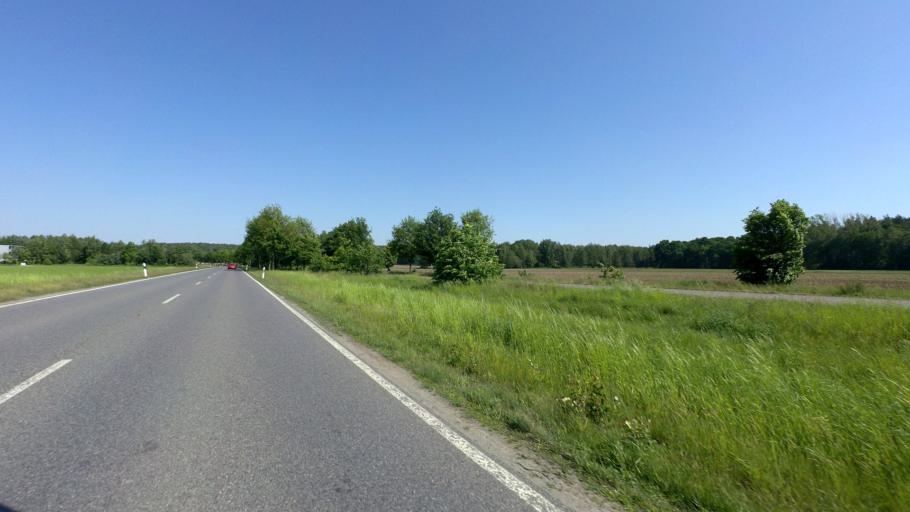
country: DE
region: Saxony
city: Kamenz
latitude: 51.2973
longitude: 14.1023
